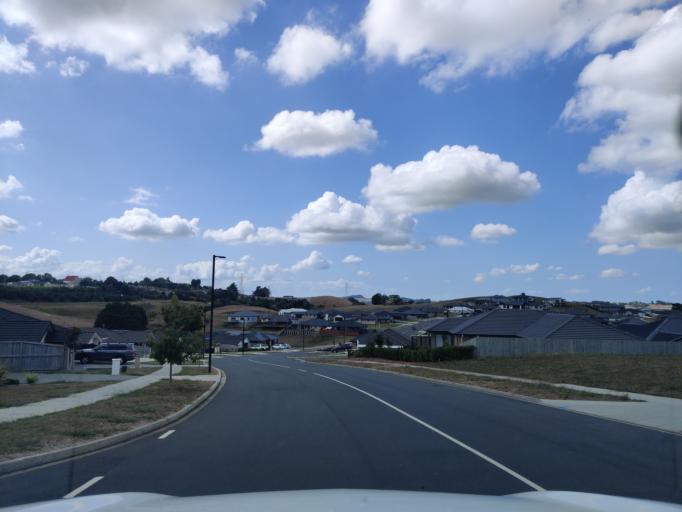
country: NZ
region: Auckland
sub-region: Auckland
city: Pukekohe East
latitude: -37.2351
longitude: 175.0155
